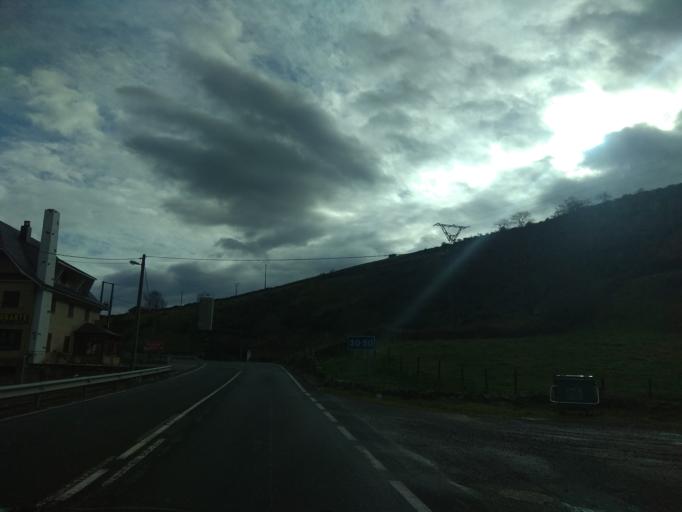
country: ES
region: Cantabria
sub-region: Provincia de Cantabria
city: San Pedro del Romeral
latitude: 43.0784
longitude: -3.8926
